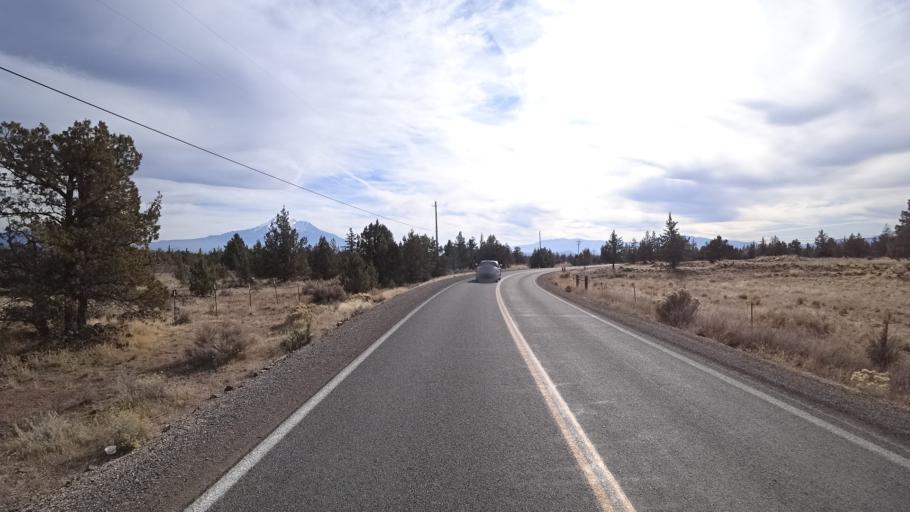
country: US
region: California
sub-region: Siskiyou County
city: Montague
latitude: 41.6434
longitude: -122.3986
